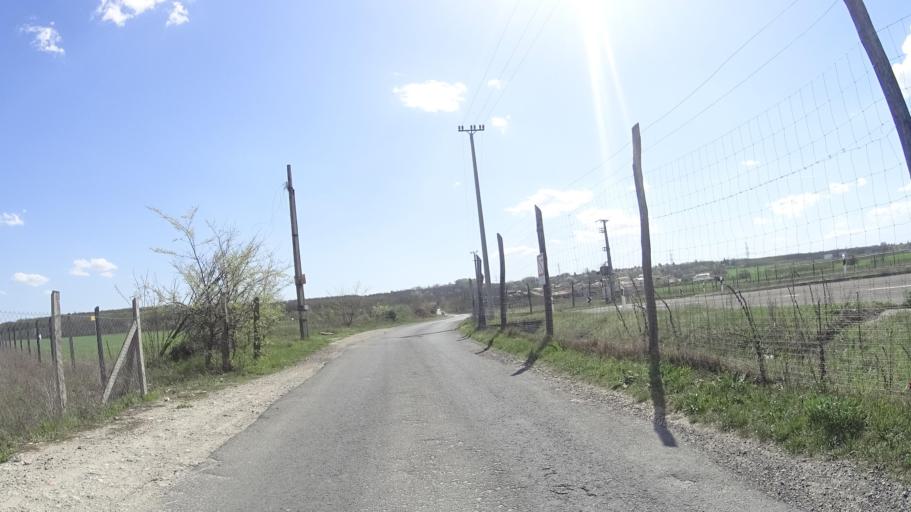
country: HU
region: Pest
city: Szada
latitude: 47.6057
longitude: 19.2962
